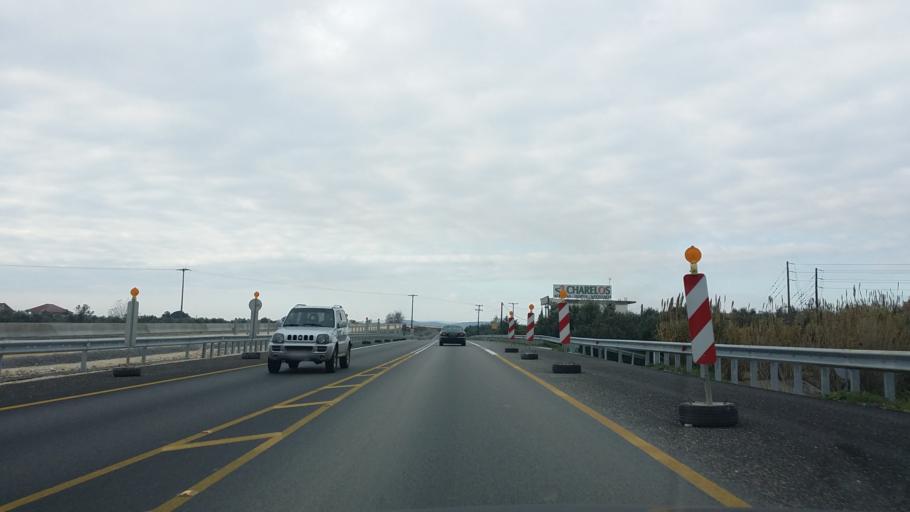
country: GR
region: West Greece
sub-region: Nomos Aitolias kai Akarnanias
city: Mesolongi
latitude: 38.3983
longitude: 21.4139
